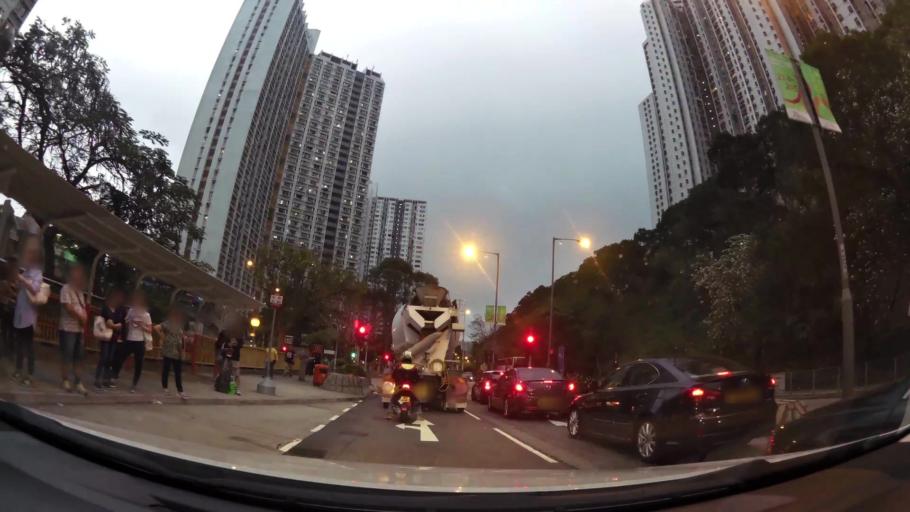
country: HK
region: Tsuen Wan
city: Tsuen Wan
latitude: 22.3495
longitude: 114.1002
